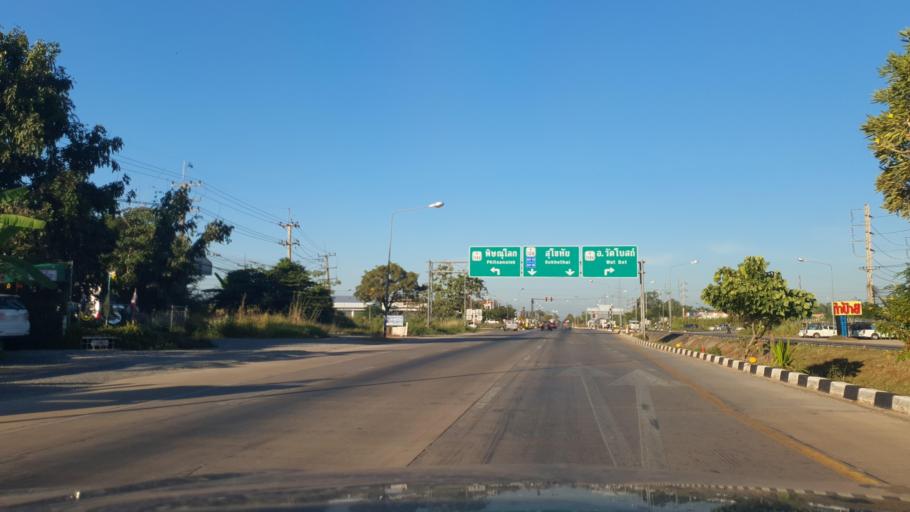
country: TH
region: Phitsanulok
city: Phitsanulok
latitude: 16.8647
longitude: 100.2511
